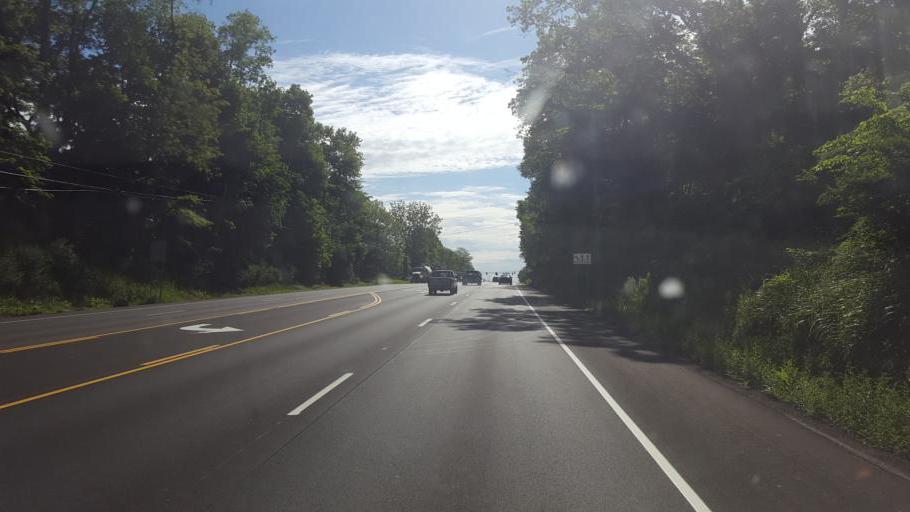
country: US
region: Ohio
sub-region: Summit County
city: Montrose-Ghent
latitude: 41.1359
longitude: -81.6718
